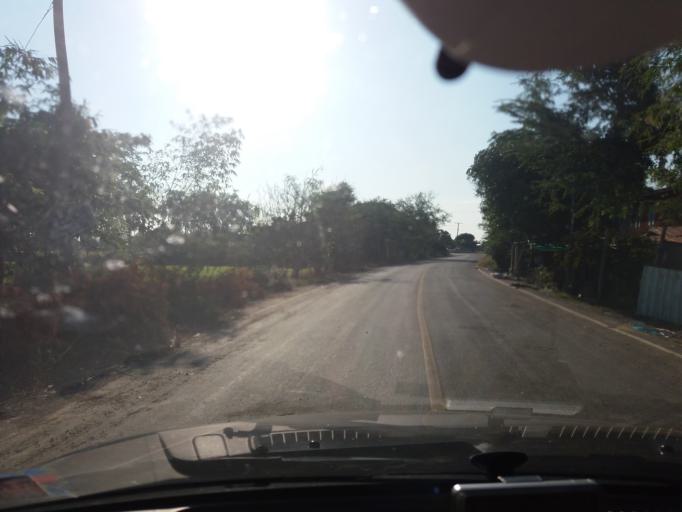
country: TH
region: Suphan Buri
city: Doem Bang Nang Buat
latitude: 14.9126
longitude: 100.1370
